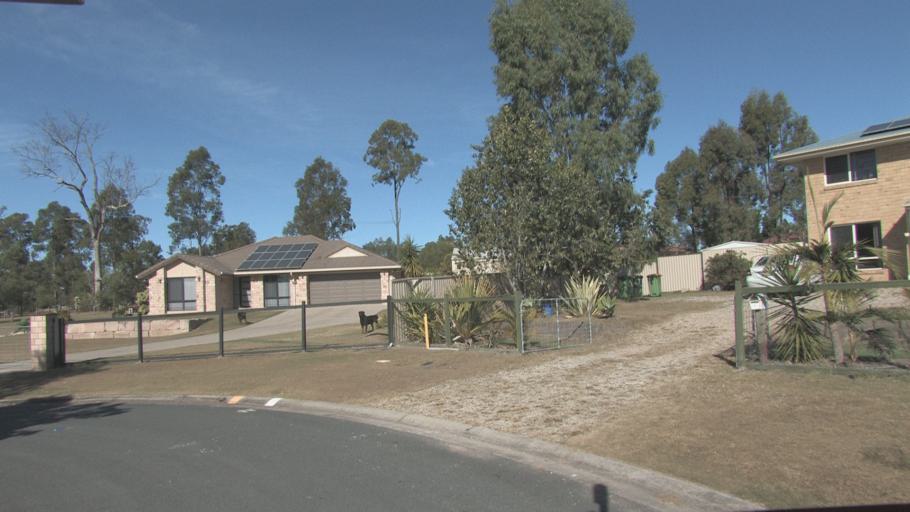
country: AU
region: Queensland
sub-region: Logan
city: North Maclean
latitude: -27.7996
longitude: 152.9637
